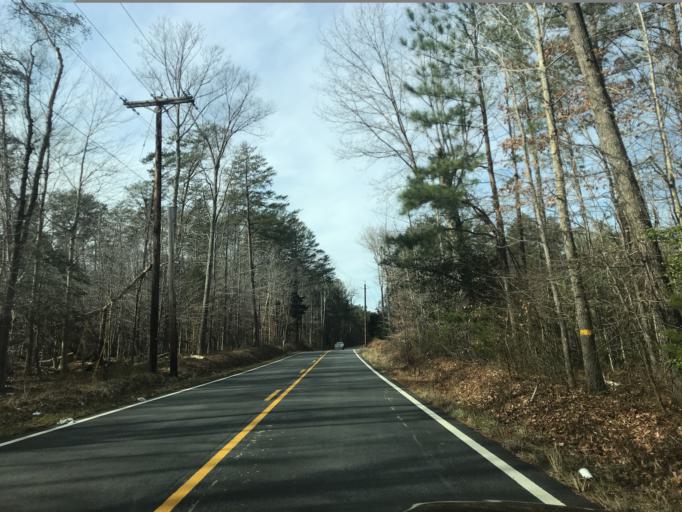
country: US
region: Virginia
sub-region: Prince William County
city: Cherry Hill
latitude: 38.4985
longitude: -77.2015
